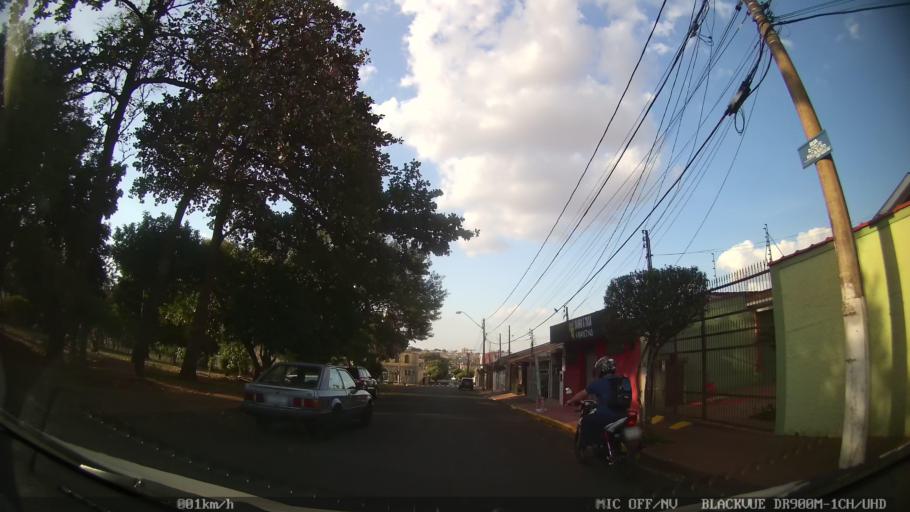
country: BR
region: Sao Paulo
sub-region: Ribeirao Preto
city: Ribeirao Preto
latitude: -21.1698
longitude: -47.8323
